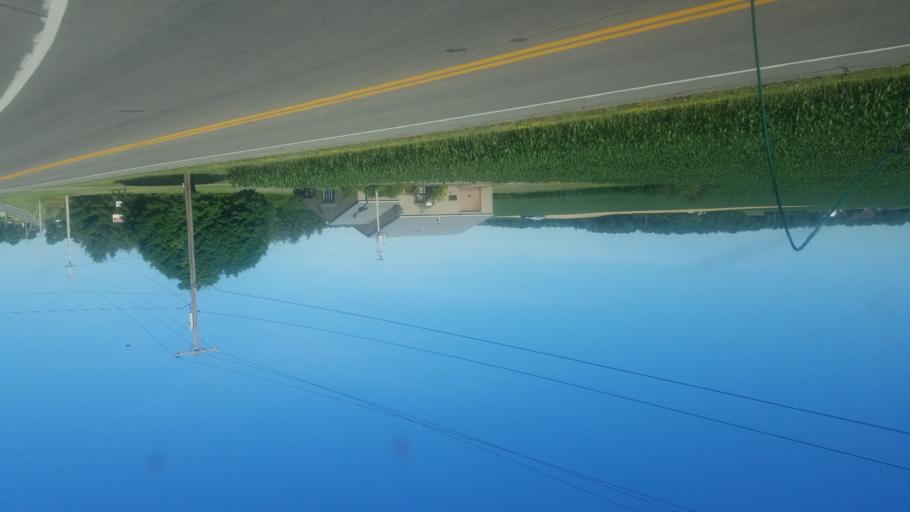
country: US
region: New York
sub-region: Ontario County
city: Phelps
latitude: 42.8865
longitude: -77.0479
